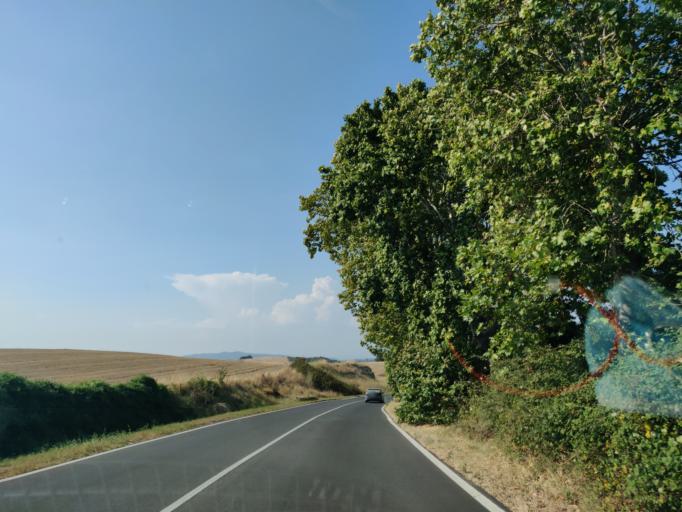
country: IT
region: Latium
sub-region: Provincia di Viterbo
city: Montalto di Castro
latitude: 42.3640
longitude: 11.6454
